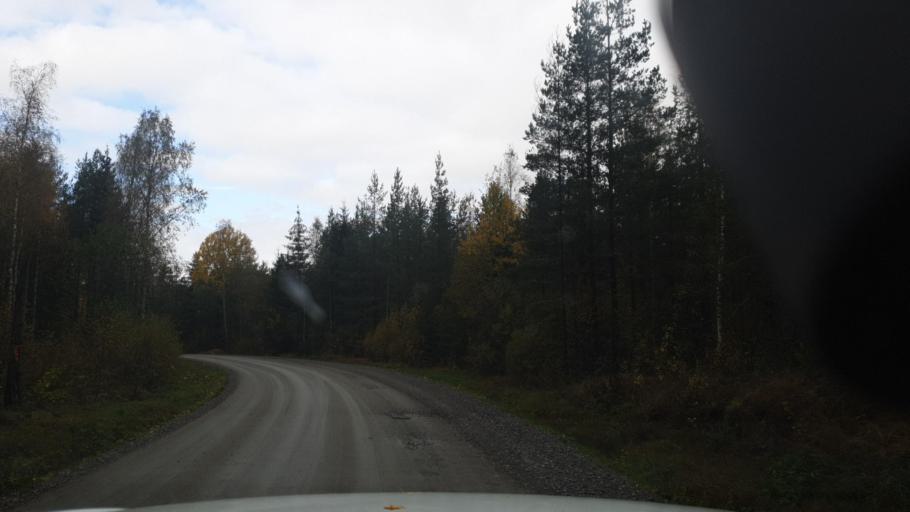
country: SE
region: Vaermland
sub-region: Karlstads Kommun
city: Valberg
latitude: 59.4518
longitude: 13.1003
